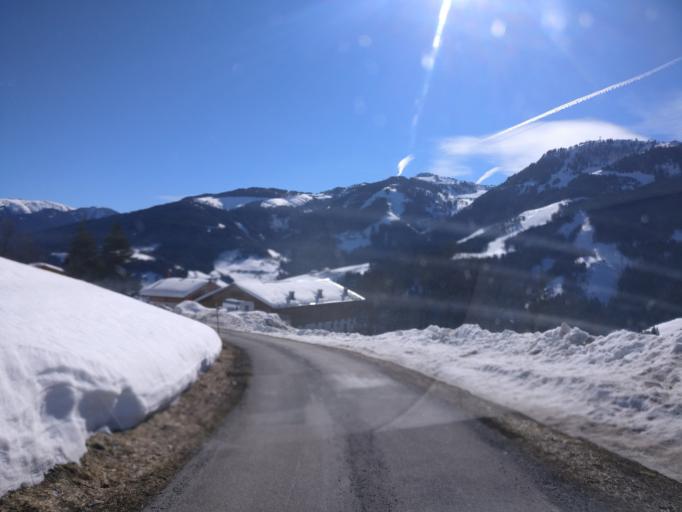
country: AT
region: Salzburg
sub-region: Politischer Bezirk Sankt Johann im Pongau
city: Sankt Johann im Pongau
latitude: 47.3378
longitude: 13.2260
